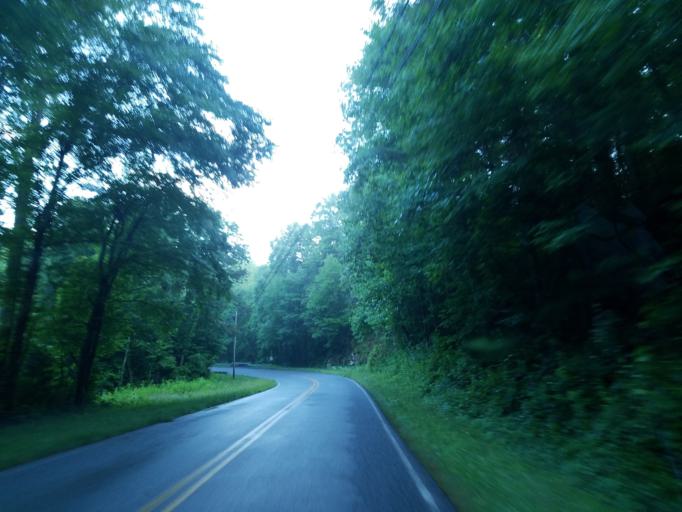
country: US
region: Georgia
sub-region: Fannin County
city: Blue Ridge
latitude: 34.7275
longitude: -84.2386
